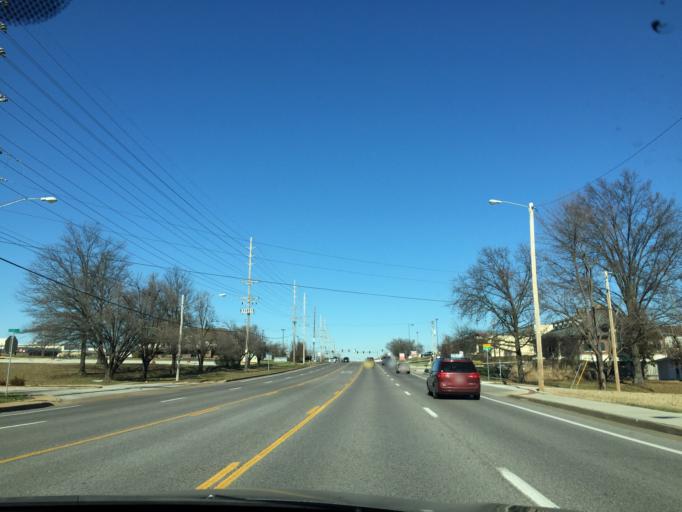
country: US
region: Missouri
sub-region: Saint Louis County
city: Ellisville
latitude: 38.6020
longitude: -90.5856
